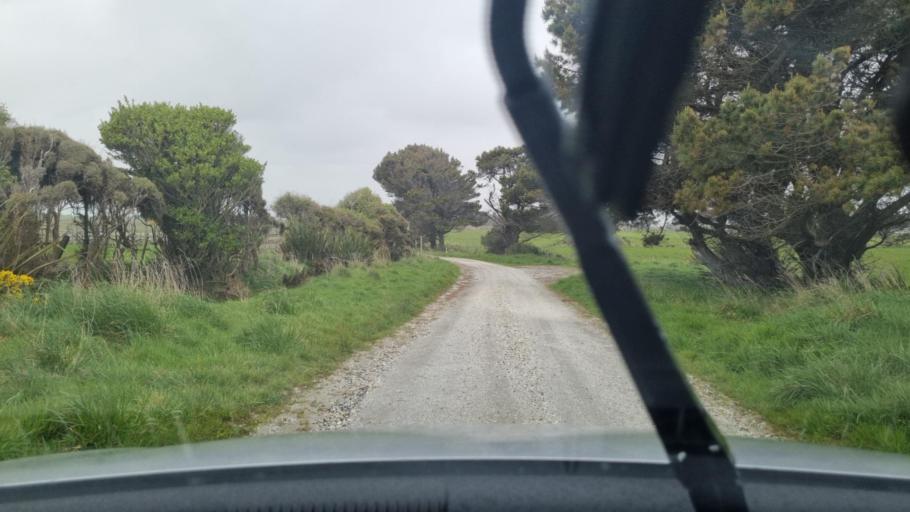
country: NZ
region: Southland
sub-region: Invercargill City
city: Bluff
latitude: -46.5201
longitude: 168.2729
